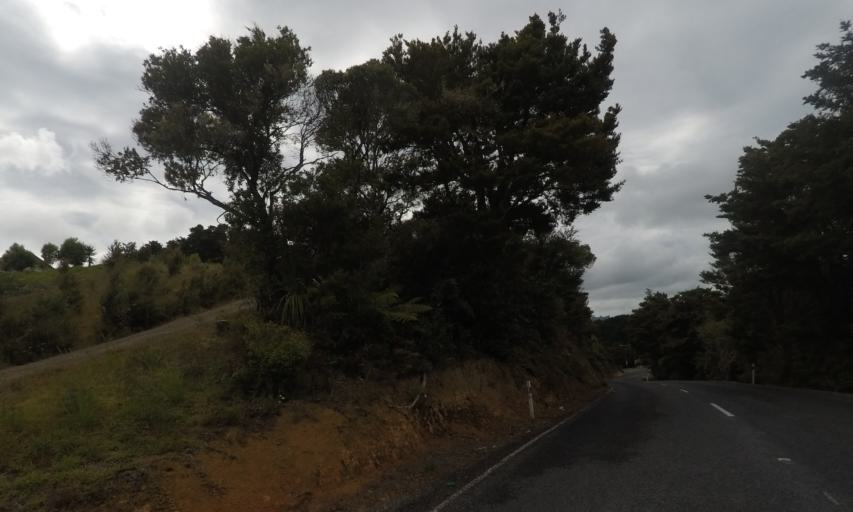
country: NZ
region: Northland
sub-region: Whangarei
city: Whangarei
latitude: -35.7581
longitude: 174.4541
